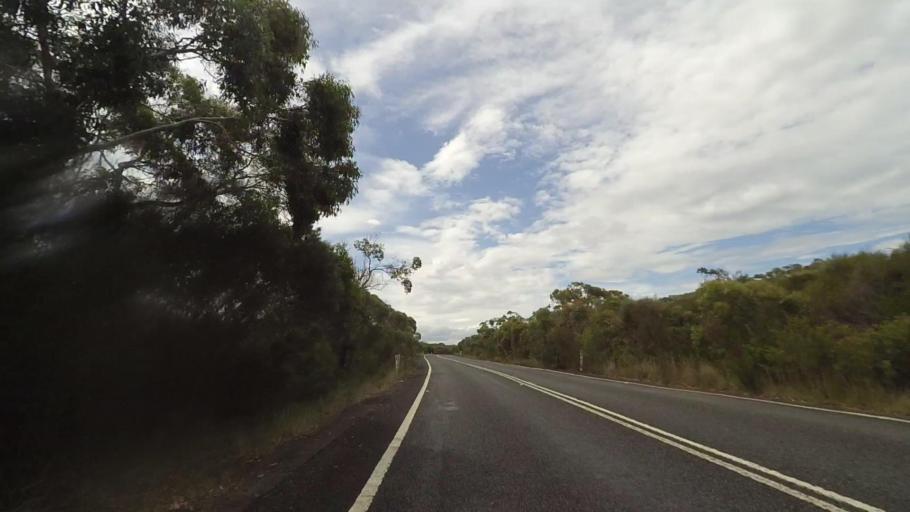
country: AU
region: New South Wales
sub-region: Sutherland Shire
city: Grays Point
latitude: -34.1247
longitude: 151.0793
